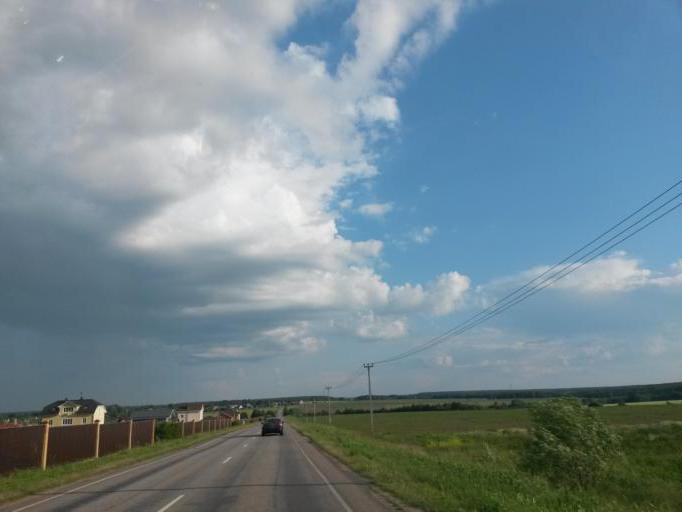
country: RU
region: Moskovskaya
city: Barybino
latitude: 55.2420
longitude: 37.7967
